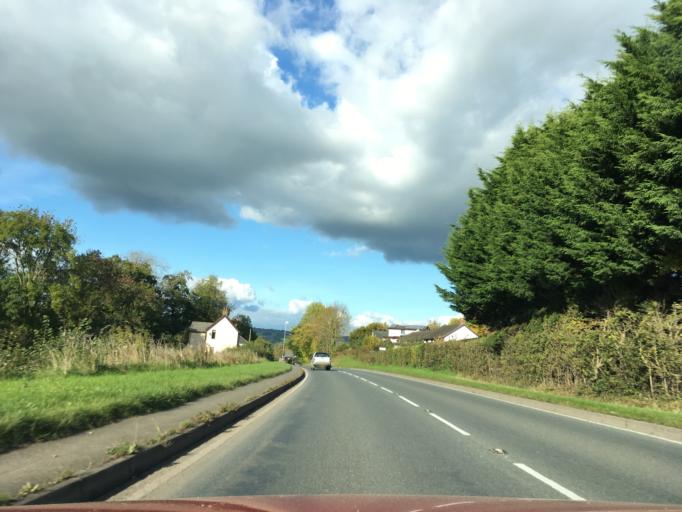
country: GB
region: Wales
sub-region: Sir Powys
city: Hay
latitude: 52.0361
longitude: -3.2027
